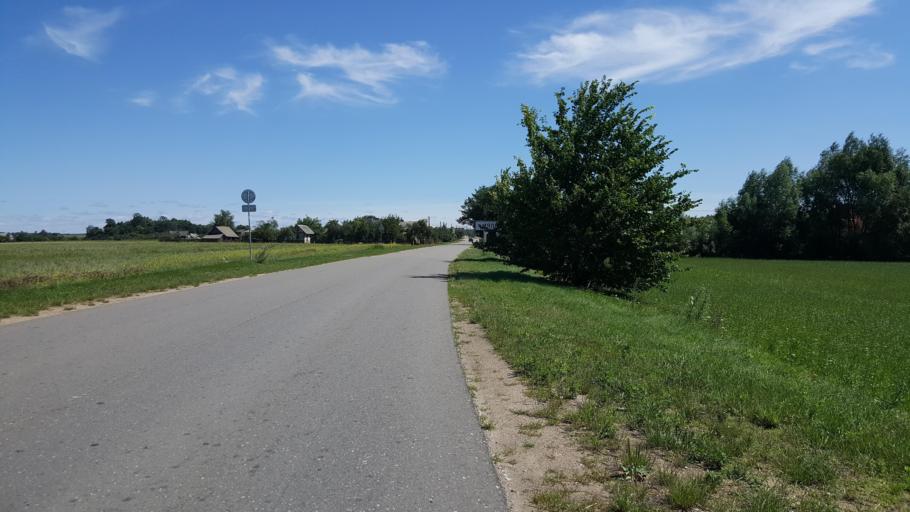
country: BY
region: Brest
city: Charnawchytsy
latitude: 52.2244
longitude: 23.7729
